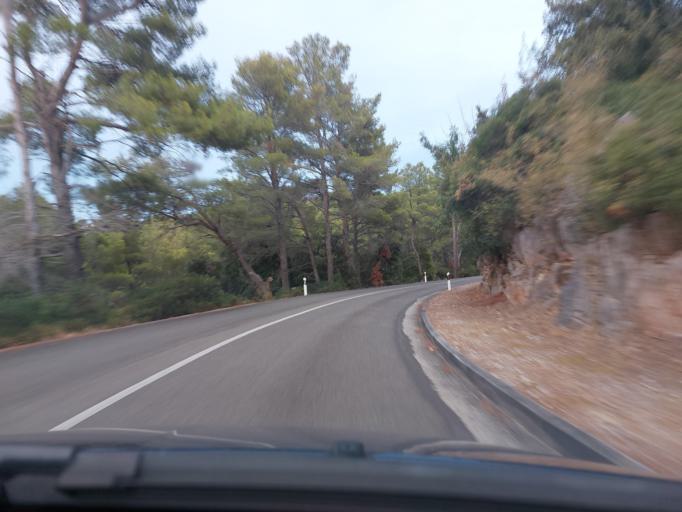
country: HR
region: Dubrovacko-Neretvanska
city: Smokvica
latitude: 42.7668
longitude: 16.8521
